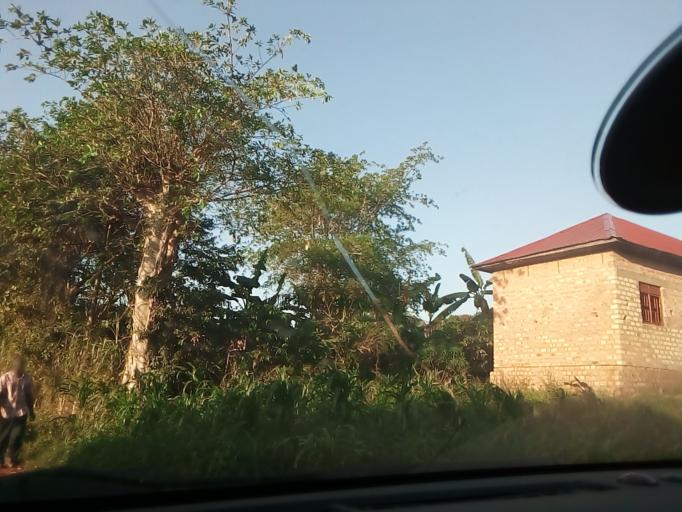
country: UG
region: Central Region
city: Masaka
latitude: -0.3392
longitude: 31.7593
